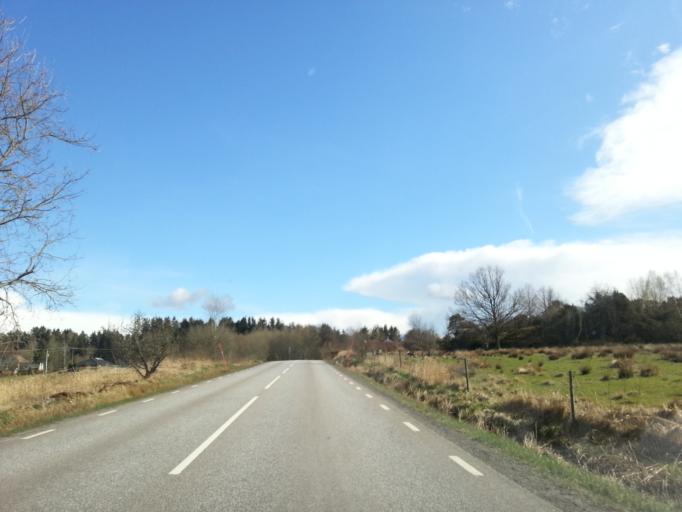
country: SE
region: Vaestra Goetaland
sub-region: Kungalvs Kommun
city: Kode
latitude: 57.9184
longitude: 11.9174
